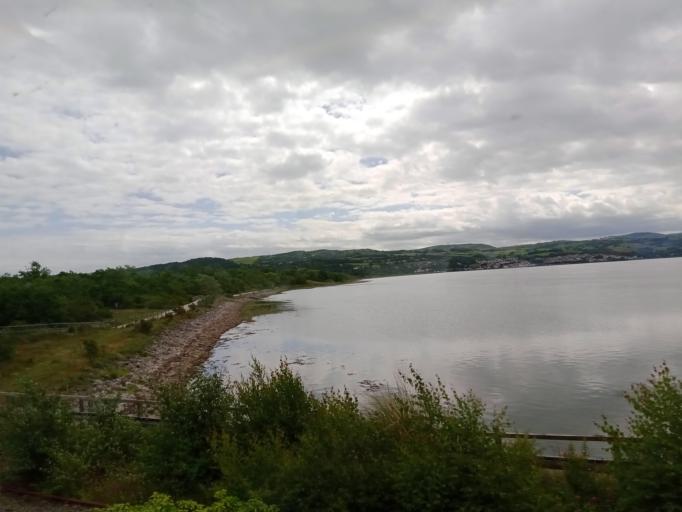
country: GB
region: Wales
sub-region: Conwy
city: Conwy
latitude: 53.2827
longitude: -3.8184
